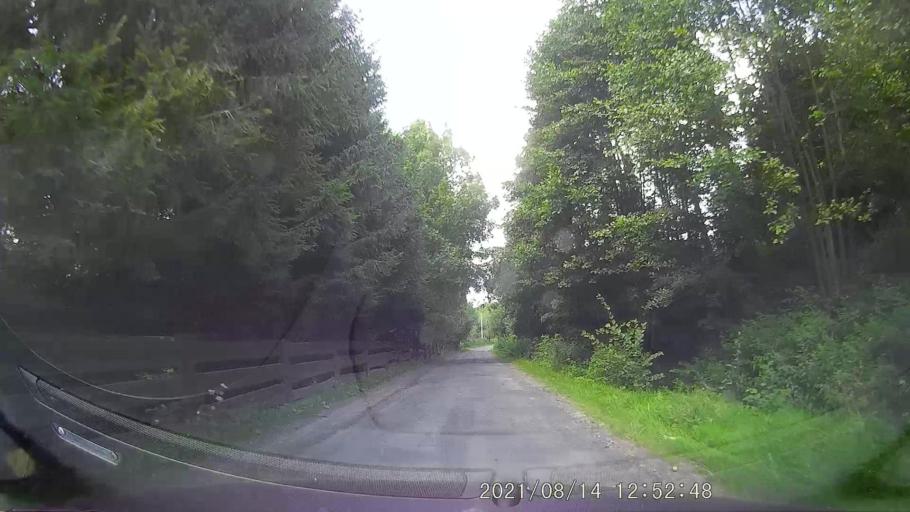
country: PL
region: Lower Silesian Voivodeship
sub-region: Powiat klodzki
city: Stronie Slaskie
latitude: 50.3189
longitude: 16.8284
